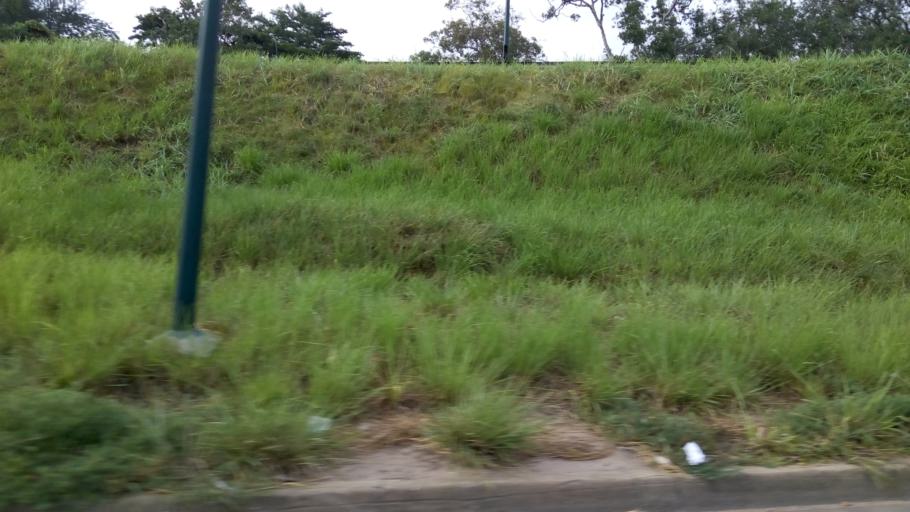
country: CI
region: Lagunes
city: Abidjan
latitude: 5.3476
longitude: -4.0065
